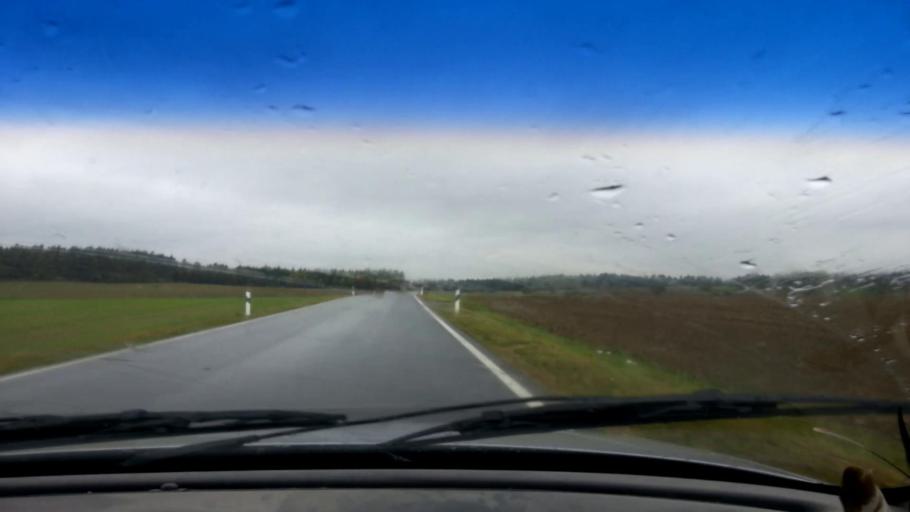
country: DE
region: Bavaria
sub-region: Upper Franconia
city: Poxdorf
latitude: 49.9117
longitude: 11.1454
